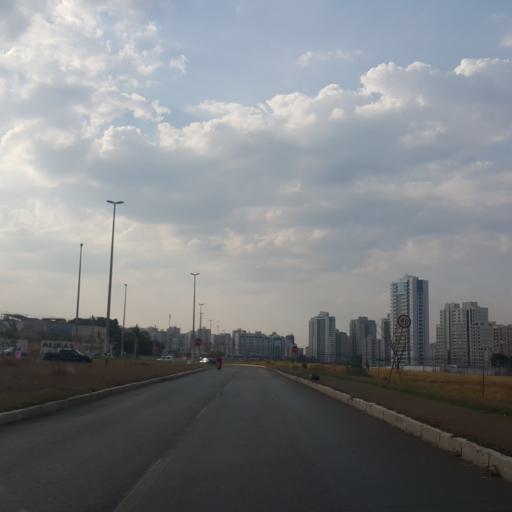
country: BR
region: Federal District
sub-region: Brasilia
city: Brasilia
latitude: -15.8530
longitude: -48.0315
